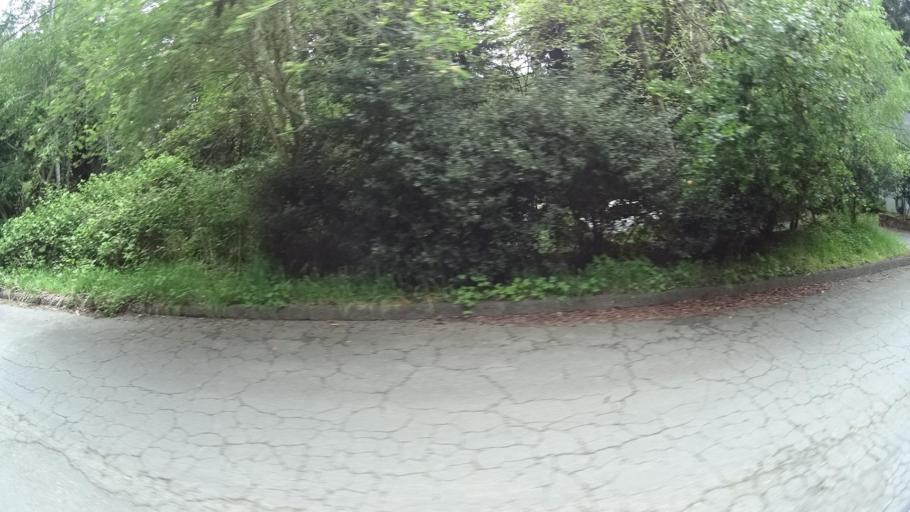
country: US
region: California
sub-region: Humboldt County
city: Arcata
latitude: 40.8623
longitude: -124.0684
